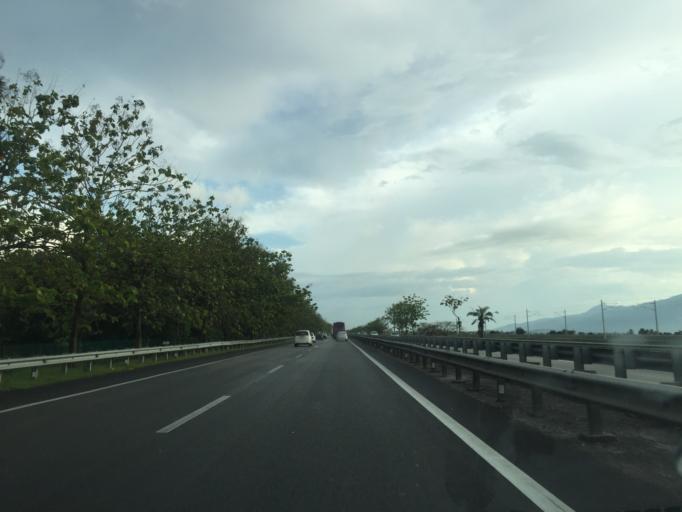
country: MY
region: Kedah
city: Gurun
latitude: 5.9317
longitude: 100.4622
